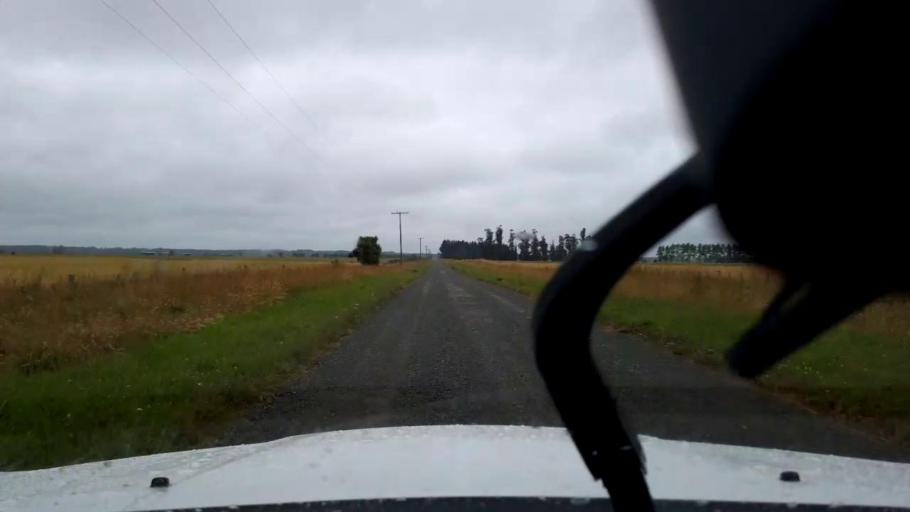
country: NZ
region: Canterbury
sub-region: Timaru District
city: Pleasant Point
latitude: -44.2332
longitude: 171.2024
